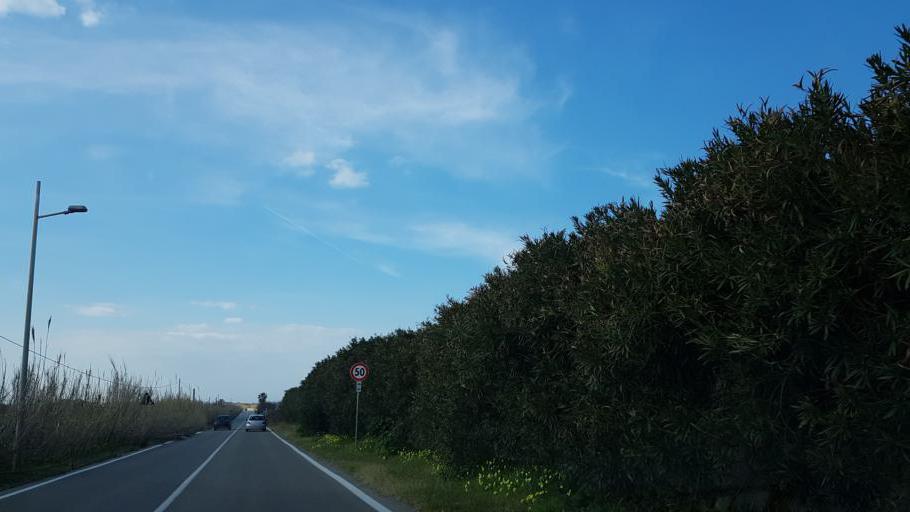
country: IT
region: Apulia
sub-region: Provincia di Brindisi
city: Brindisi
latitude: 40.6820
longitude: 17.8888
